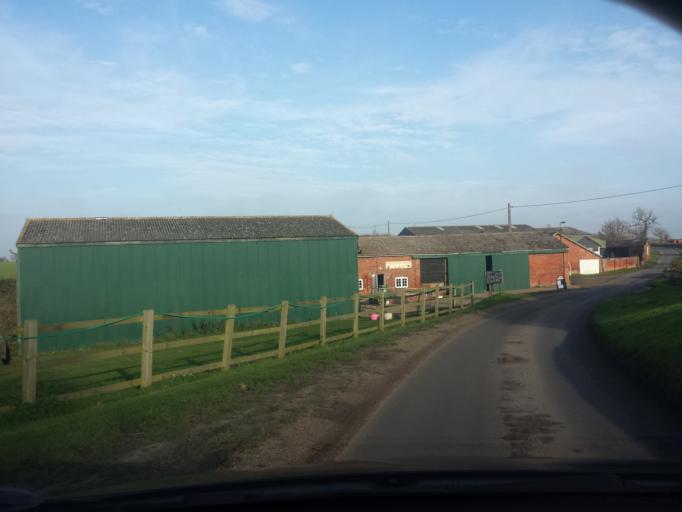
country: GB
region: England
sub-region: Essex
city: Saint Osyth
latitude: 51.8217
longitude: 1.0760
